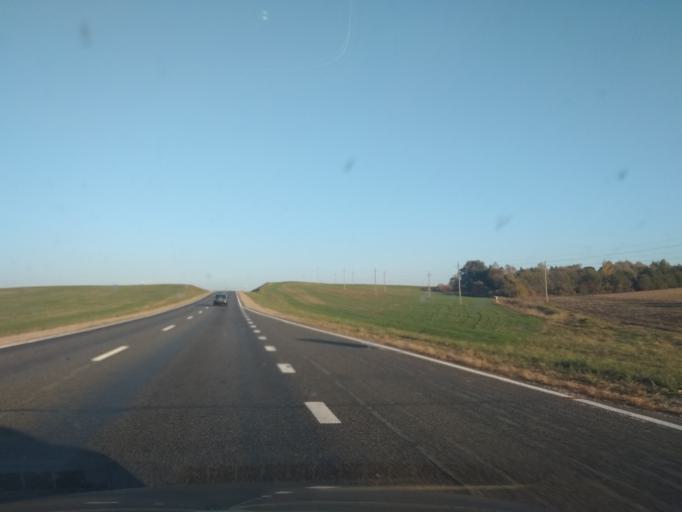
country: BY
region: Grodnenskaya
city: Zel'va
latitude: 53.1414
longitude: 24.7609
